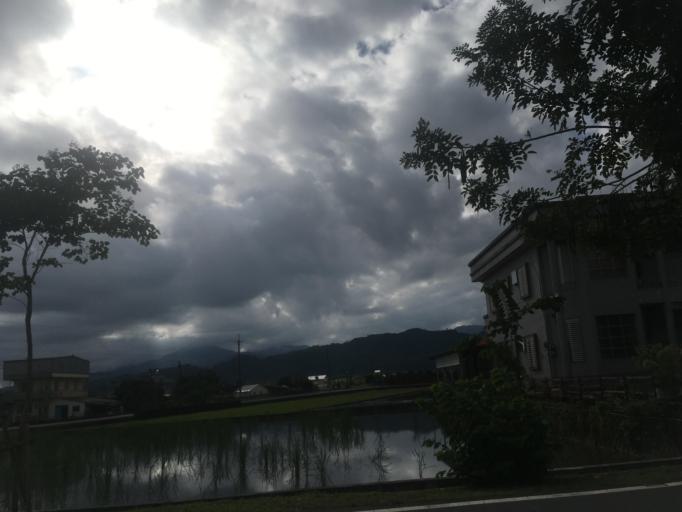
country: TW
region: Taiwan
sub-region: Yilan
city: Yilan
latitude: 24.6795
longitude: 121.6839
